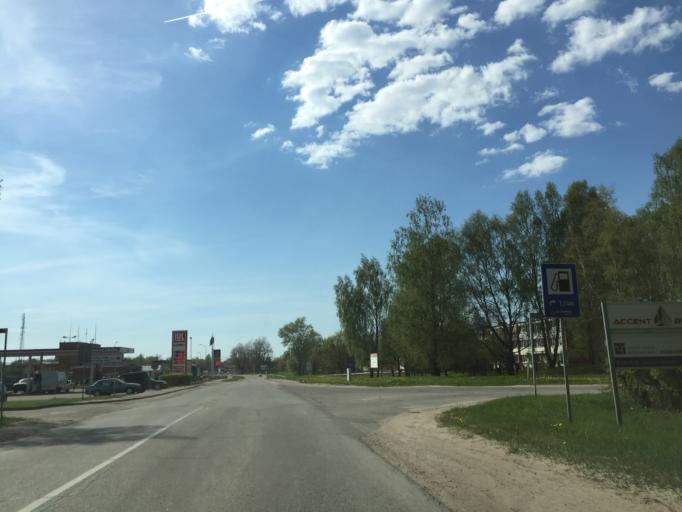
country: LV
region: Limbazu Rajons
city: Limbazi
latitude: 57.5124
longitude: 24.7309
